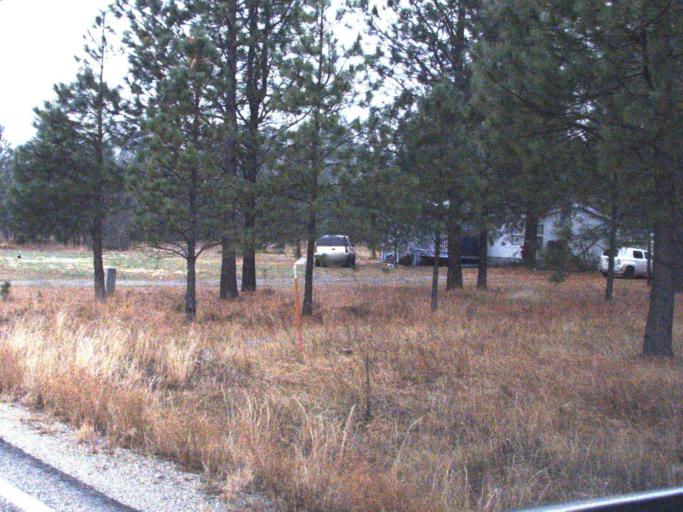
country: CA
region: British Columbia
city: Grand Forks
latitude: 48.9924
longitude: -118.2255
